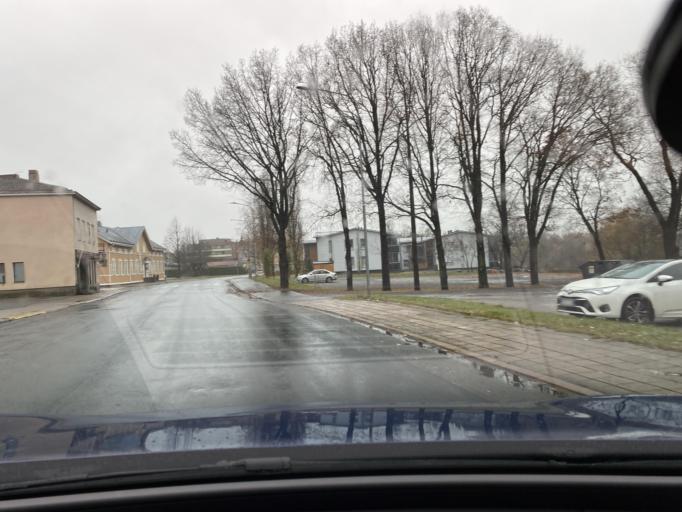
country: FI
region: Varsinais-Suomi
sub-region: Loimaa
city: Loimaa
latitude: 60.8524
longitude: 23.0596
